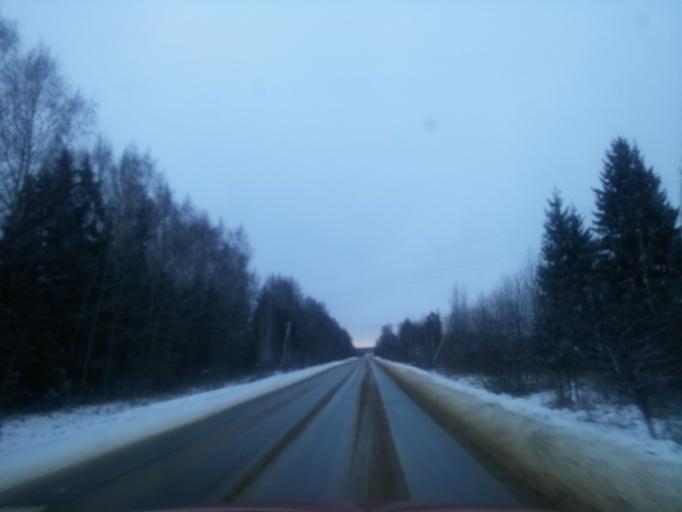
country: RU
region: Tverskaya
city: Likhoslavl'
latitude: 56.9972
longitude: 35.4474
